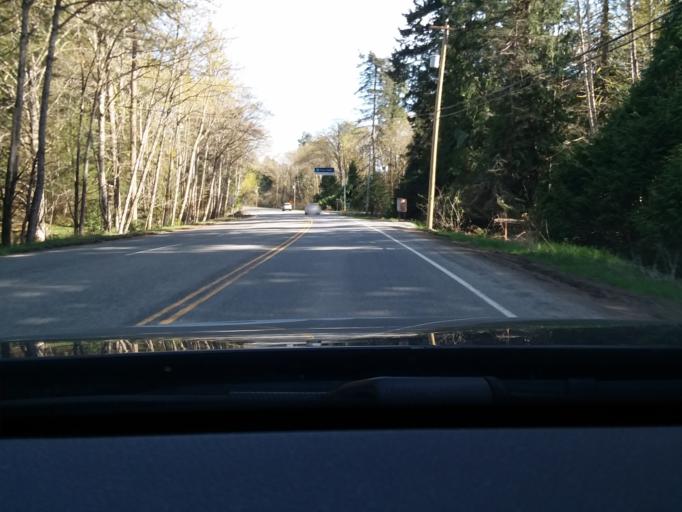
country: CA
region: British Columbia
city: North Saanich
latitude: 48.8510
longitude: -123.4529
